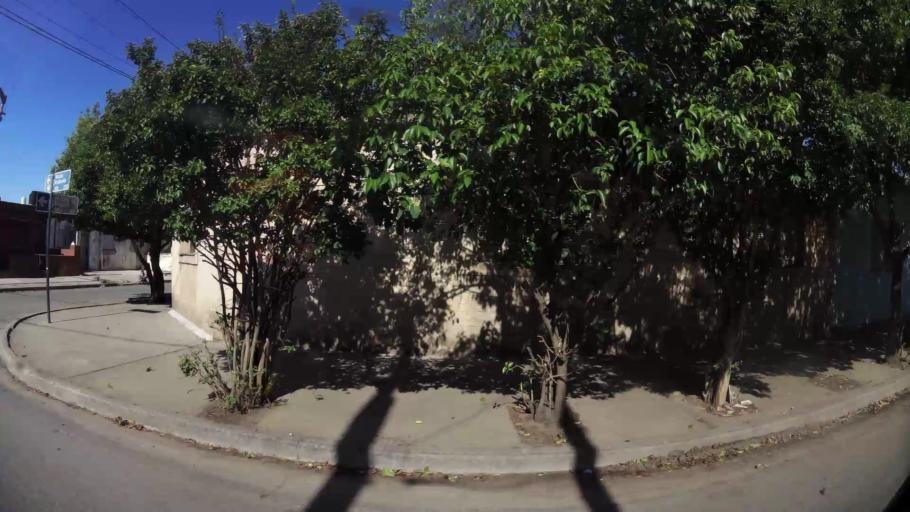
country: AR
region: Cordoba
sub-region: Departamento de Capital
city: Cordoba
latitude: -31.3700
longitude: -64.1869
